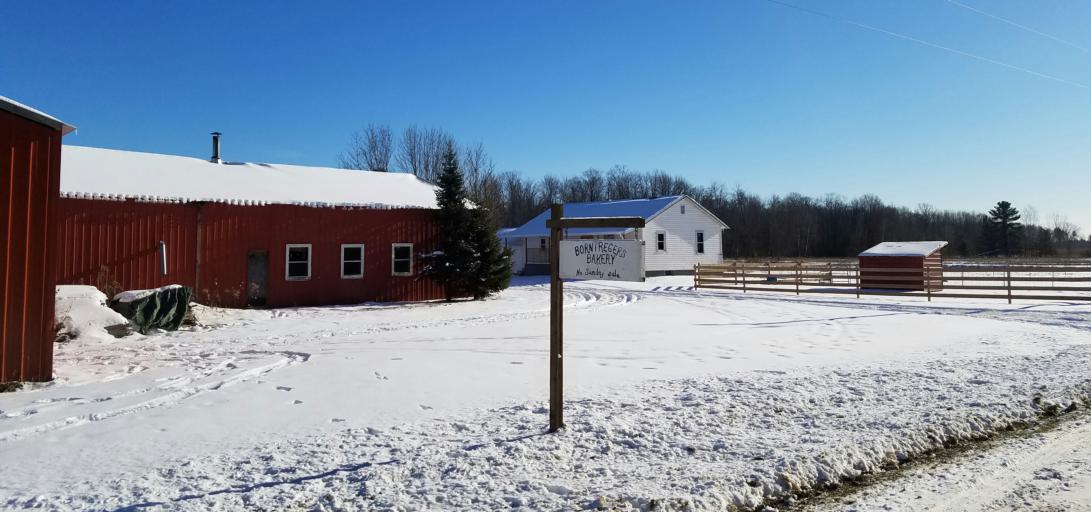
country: US
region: Wisconsin
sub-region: Marathon County
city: Spencer
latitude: 44.5646
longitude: -90.3763
